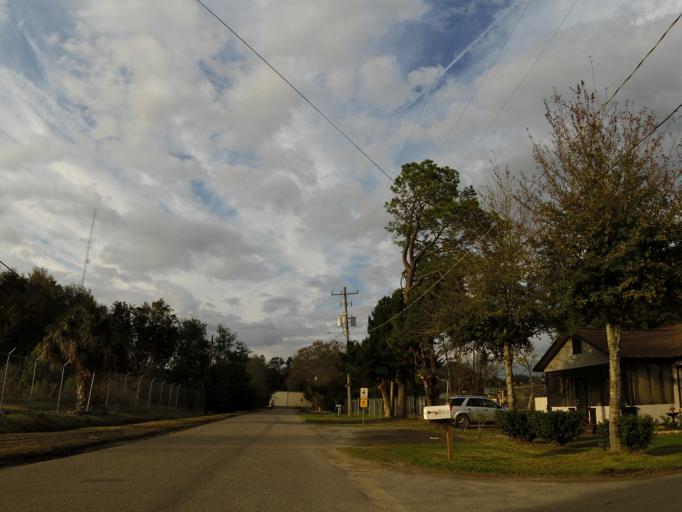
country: US
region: Florida
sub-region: Duval County
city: Jacksonville
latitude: 30.3269
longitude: -81.7455
